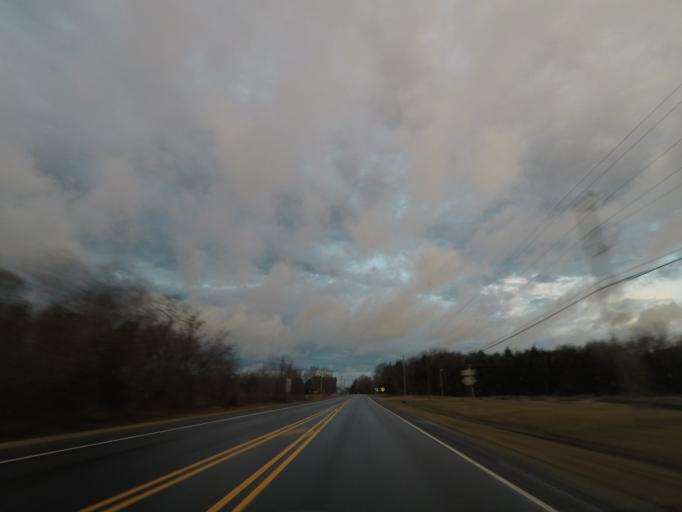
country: US
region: North Carolina
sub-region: Alamance County
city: Mebane
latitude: 36.2467
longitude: -79.1898
